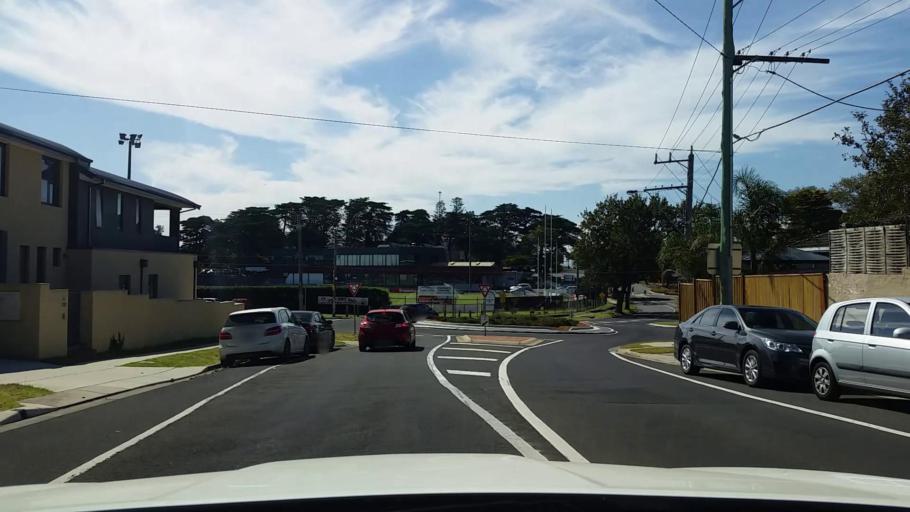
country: AU
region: Victoria
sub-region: Frankston
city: Frankston
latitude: -38.1490
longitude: 145.1204
